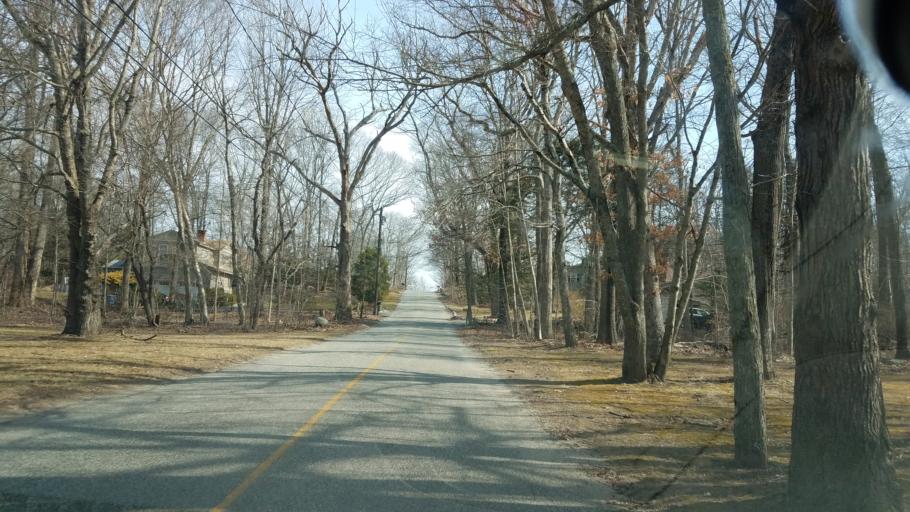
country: US
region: Connecticut
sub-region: New London County
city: Preston City
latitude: 41.5018
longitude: -72.0020
